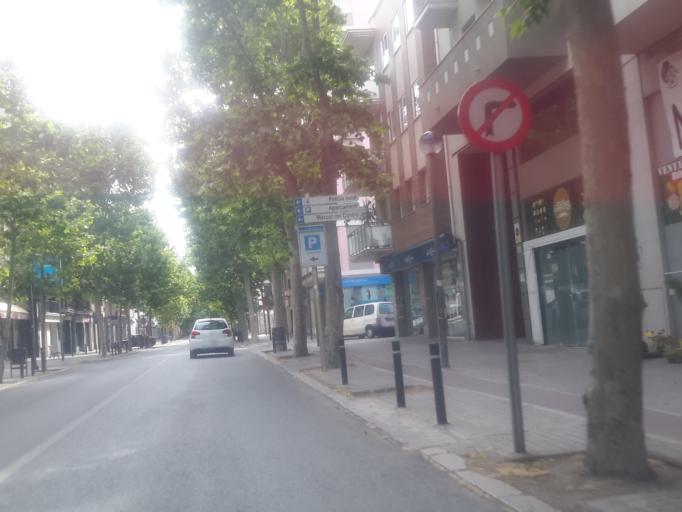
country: ES
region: Catalonia
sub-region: Provincia de Barcelona
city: Vilanova i la Geltru
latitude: 41.2198
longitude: 1.7229
